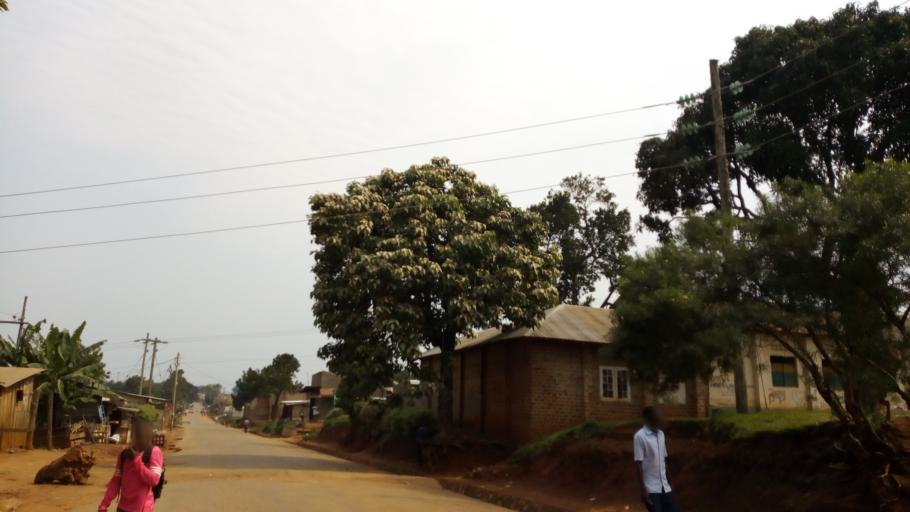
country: UG
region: Central Region
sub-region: Wakiso District
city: Kireka
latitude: 0.3072
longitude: 32.6524
